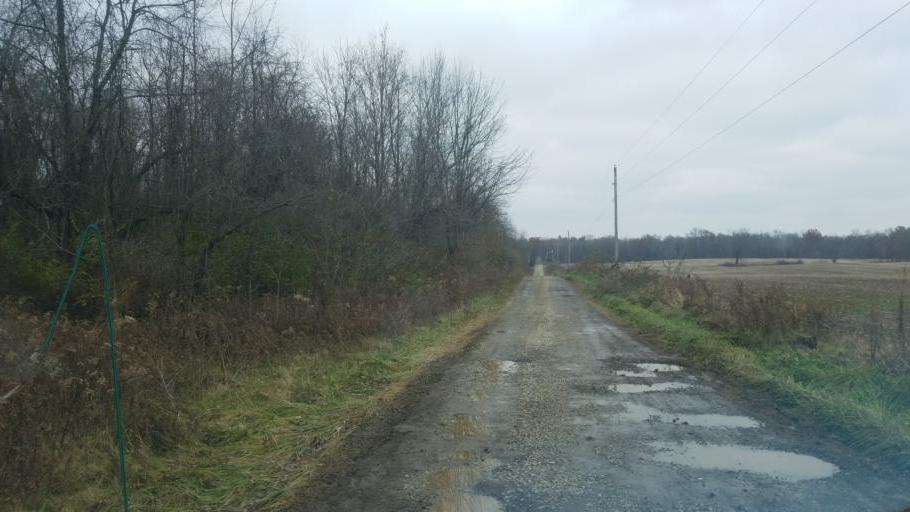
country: US
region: Ohio
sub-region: Morrow County
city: Cardington
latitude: 40.4373
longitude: -82.8396
